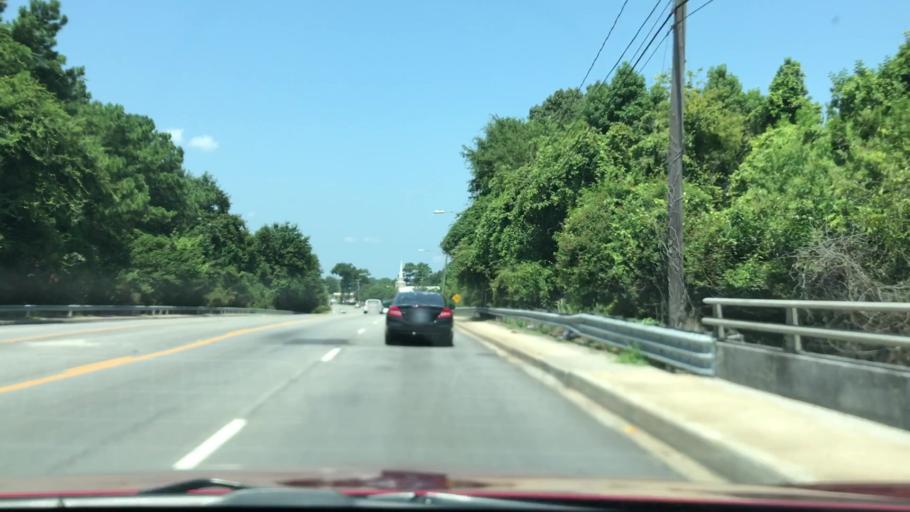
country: US
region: South Carolina
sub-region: Charleston County
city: North Charleston
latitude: 32.8562
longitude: -80.0255
